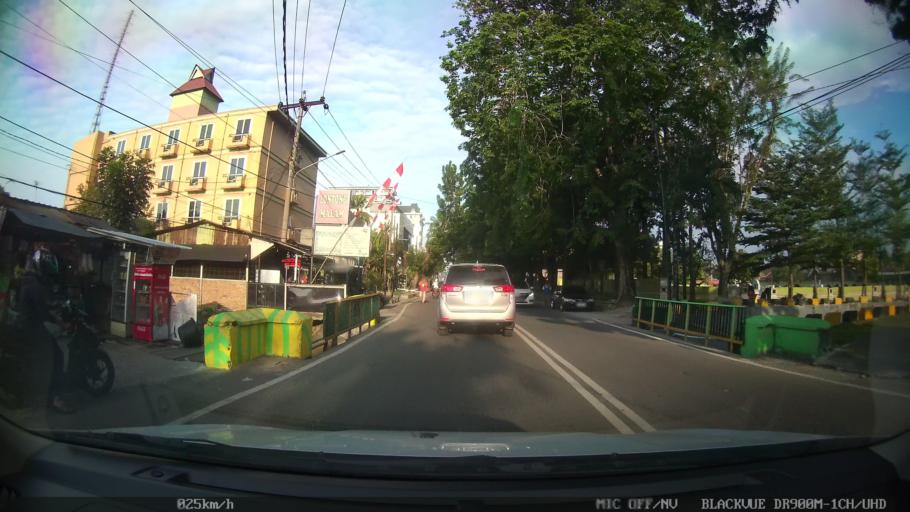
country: ID
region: North Sumatra
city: Medan
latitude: 3.5770
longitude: 98.6552
